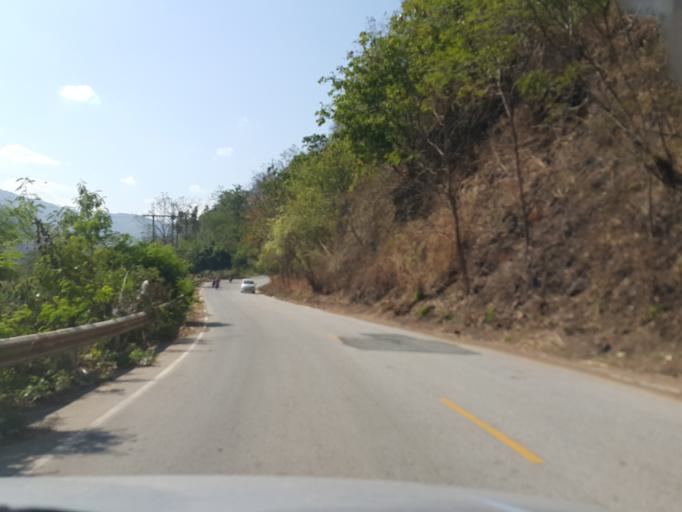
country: TH
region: Chiang Mai
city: Mae Wang
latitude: 18.6174
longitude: 98.7541
